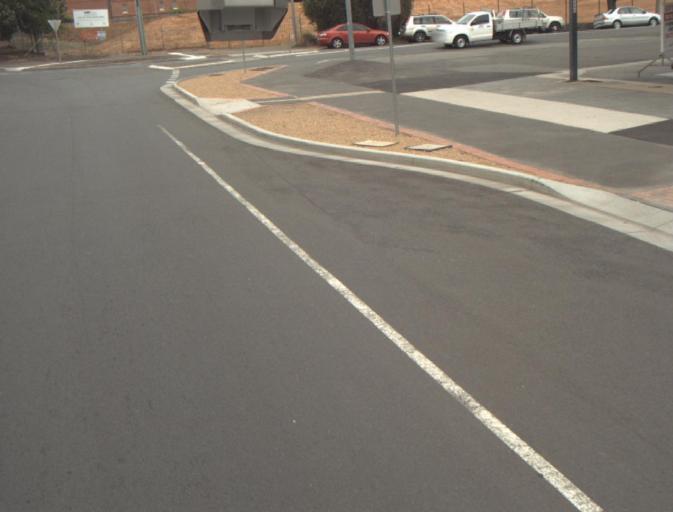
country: AU
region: Tasmania
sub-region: Launceston
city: Launceston
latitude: -41.4298
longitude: 147.1384
